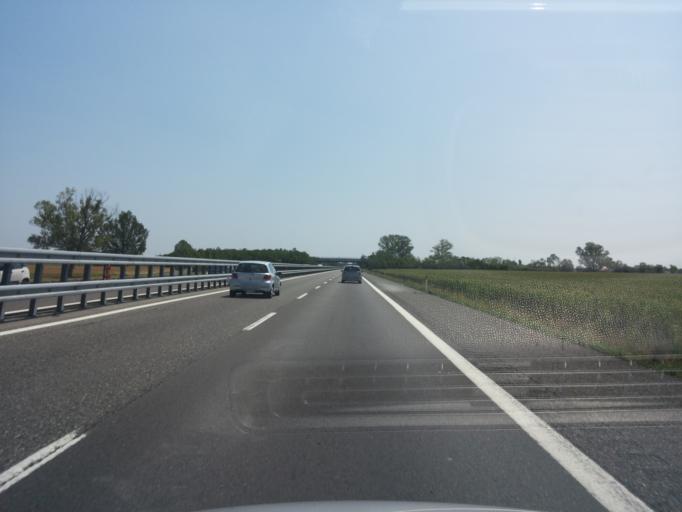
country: IT
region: Emilia-Romagna
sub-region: Provincia di Piacenza
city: Sarmato
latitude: 45.0684
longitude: 9.5100
